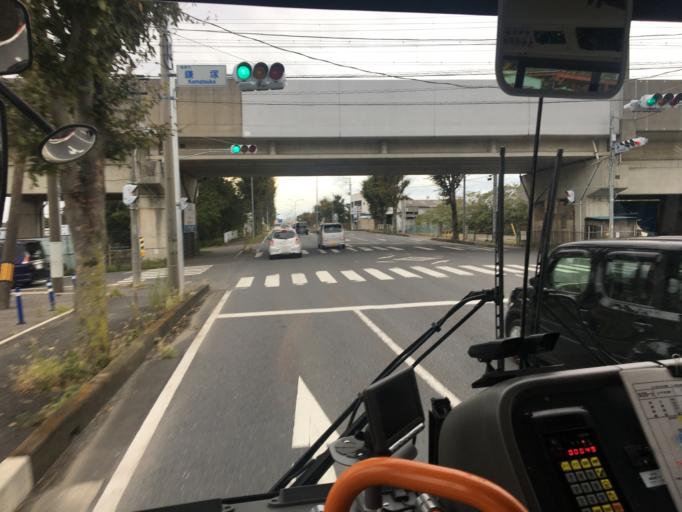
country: JP
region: Saitama
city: Fukiage-fujimi
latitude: 36.1123
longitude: 139.4594
